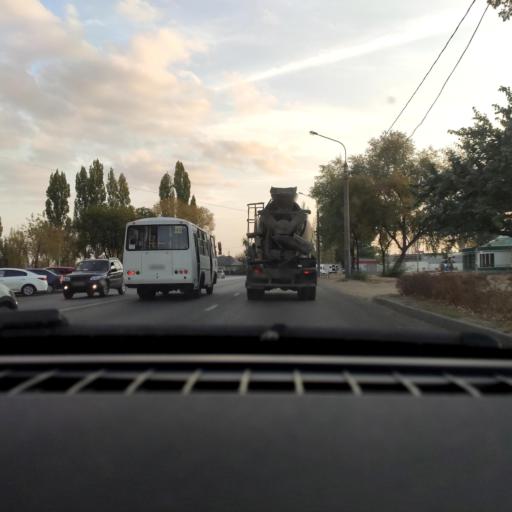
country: RU
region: Voronezj
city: Maslovka
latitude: 51.6351
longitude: 39.2635
